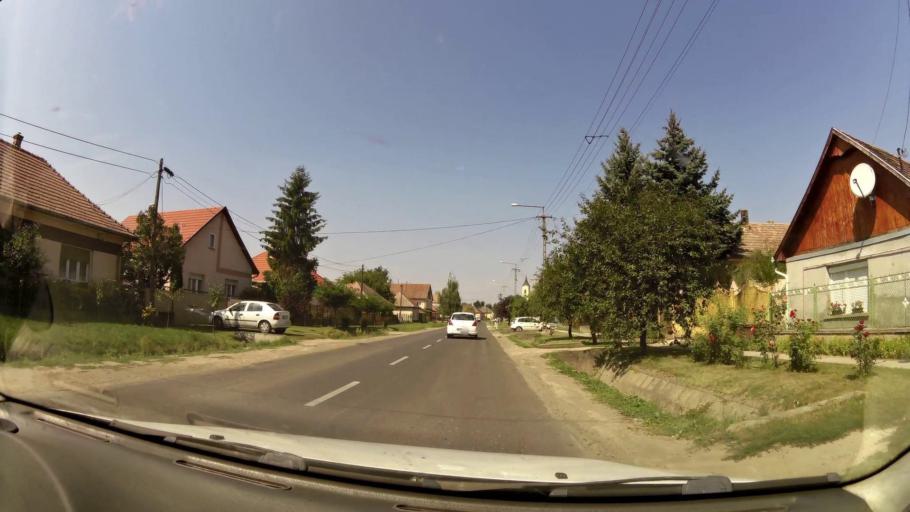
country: HU
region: Pest
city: Tapiobicske
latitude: 47.3600
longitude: 19.6909
